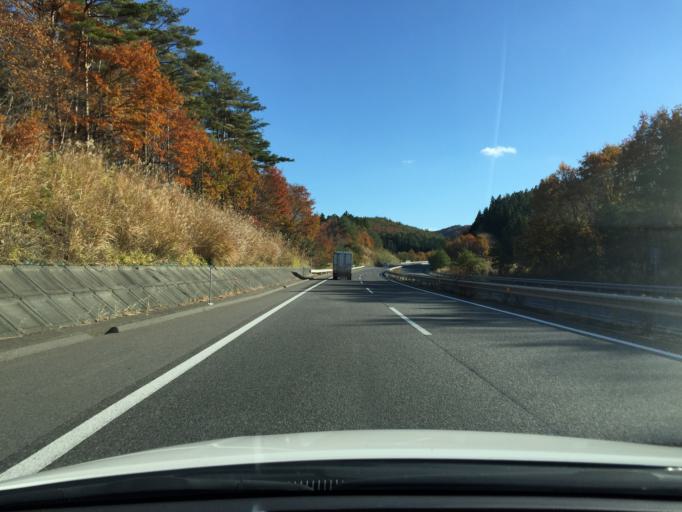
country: JP
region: Fukushima
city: Iwaki
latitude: 37.2087
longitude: 140.6934
